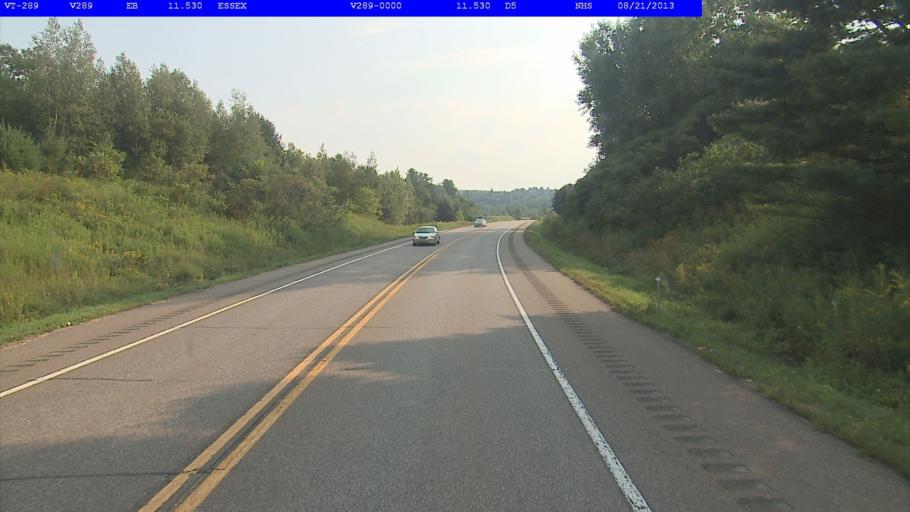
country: US
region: Vermont
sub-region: Chittenden County
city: Essex Junction
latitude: 44.4865
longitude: -73.0645
